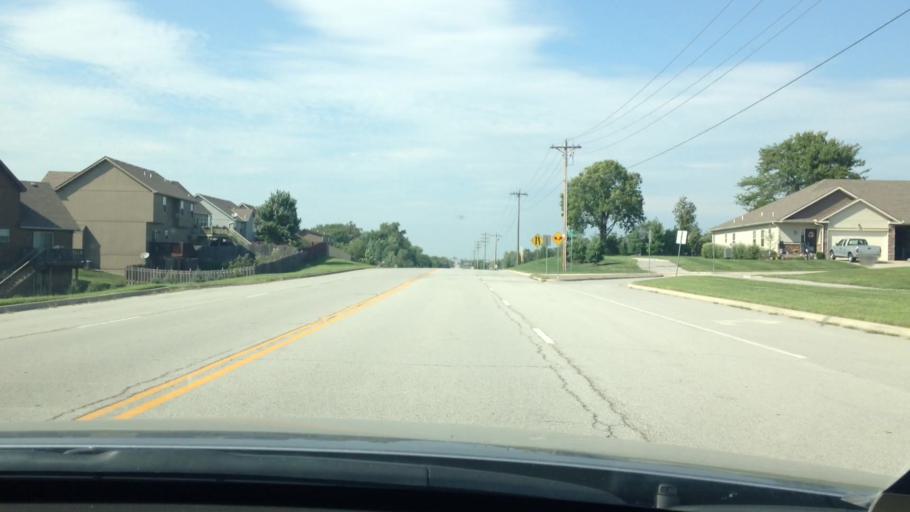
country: US
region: Missouri
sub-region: Platte County
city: Platte City
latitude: 39.3175
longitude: -94.7611
